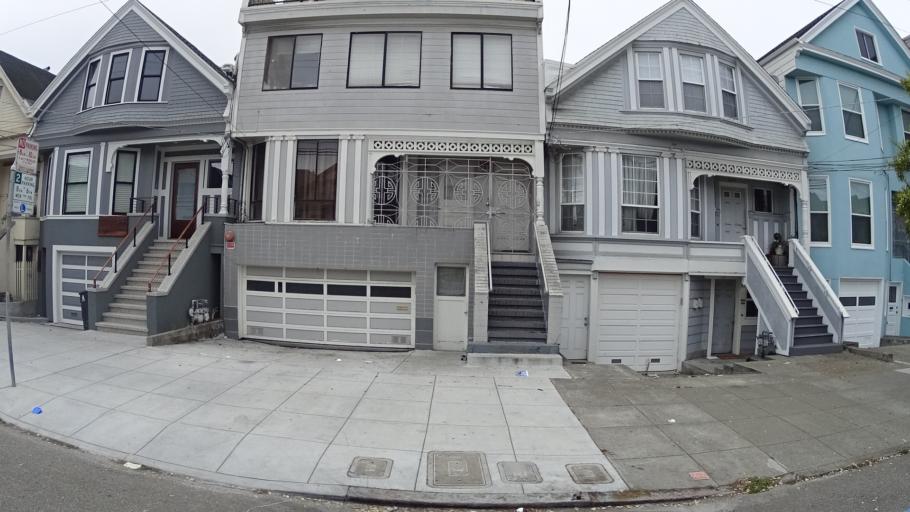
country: US
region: California
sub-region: San Francisco County
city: San Francisco
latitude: 37.7791
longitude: -122.4599
